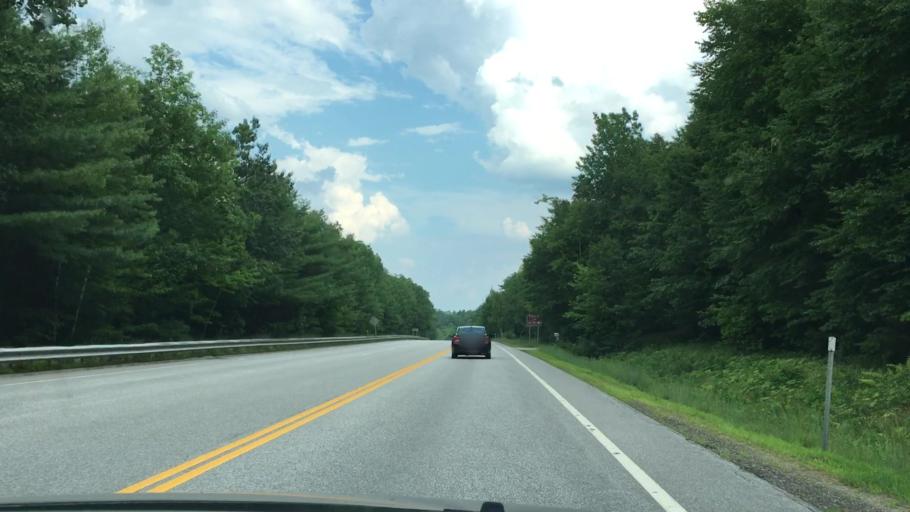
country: US
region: New Hampshire
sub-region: Belknap County
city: Gilford
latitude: 43.5747
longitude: -71.3636
